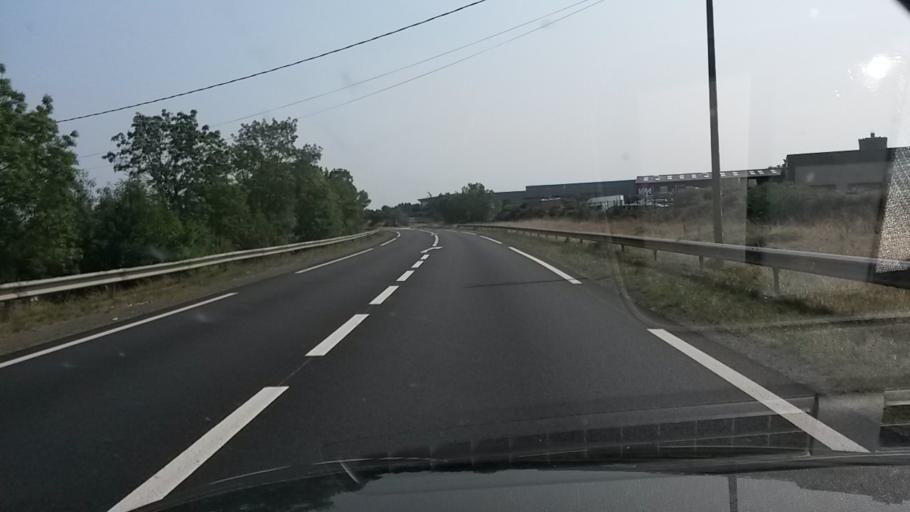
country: FR
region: Pays de la Loire
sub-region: Departement de la Loire-Atlantique
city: Ancenis
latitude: 47.3794
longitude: -1.1724
